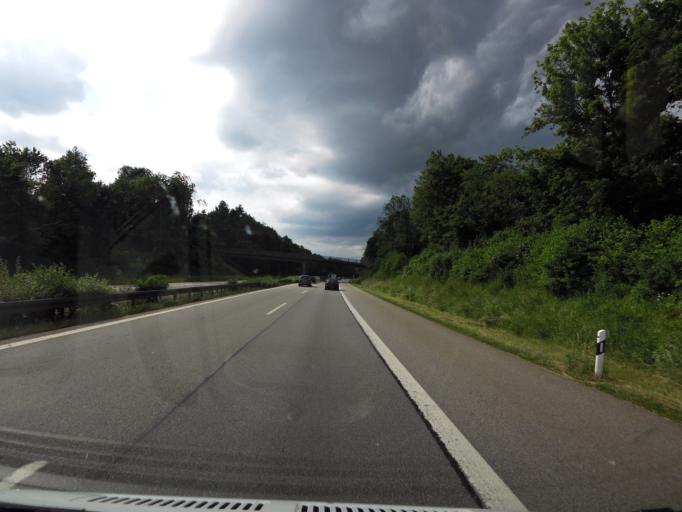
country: DE
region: Bavaria
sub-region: Lower Bavaria
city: Aussernzell
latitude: 48.6897
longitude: 13.2016
